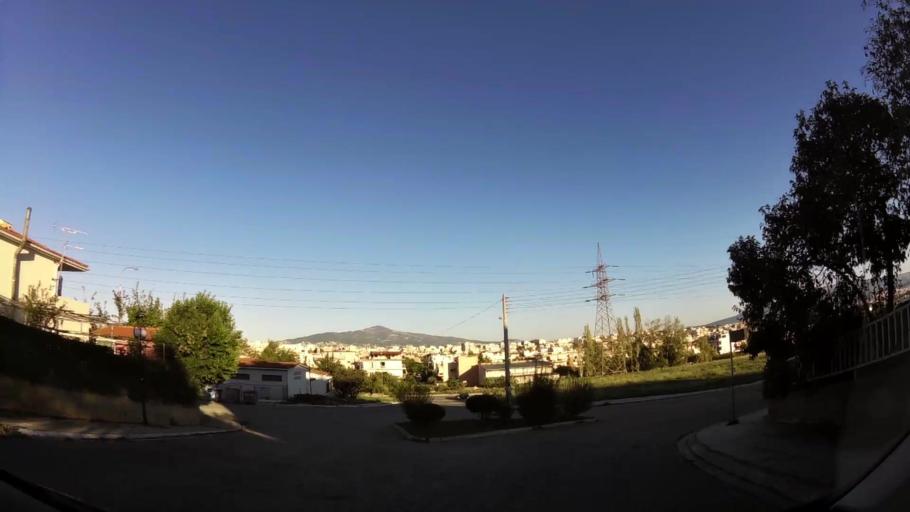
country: GR
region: Attica
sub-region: Nomarchia Anatolikis Attikis
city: Acharnes
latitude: 38.0828
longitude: 23.7248
